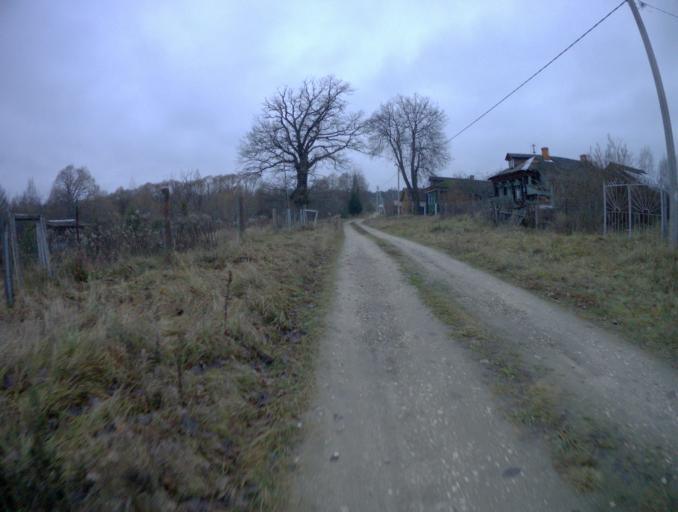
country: RU
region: Vladimir
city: Golovino
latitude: 55.9921
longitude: 40.5269
